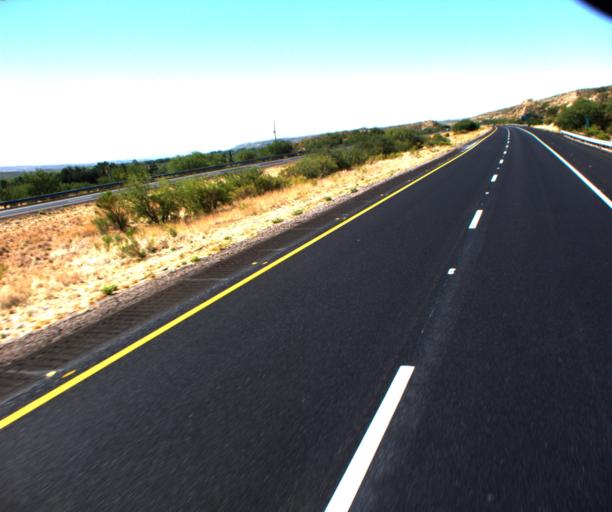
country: US
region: Arizona
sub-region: Santa Cruz County
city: Tubac
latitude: 31.5812
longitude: -111.0552
